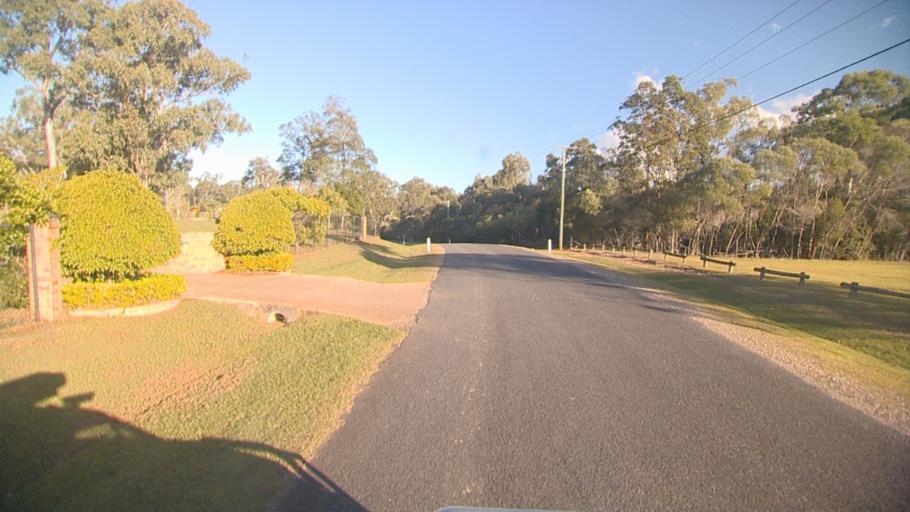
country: AU
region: Queensland
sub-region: Redland
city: Redland Bay
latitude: -27.6615
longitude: 153.2674
